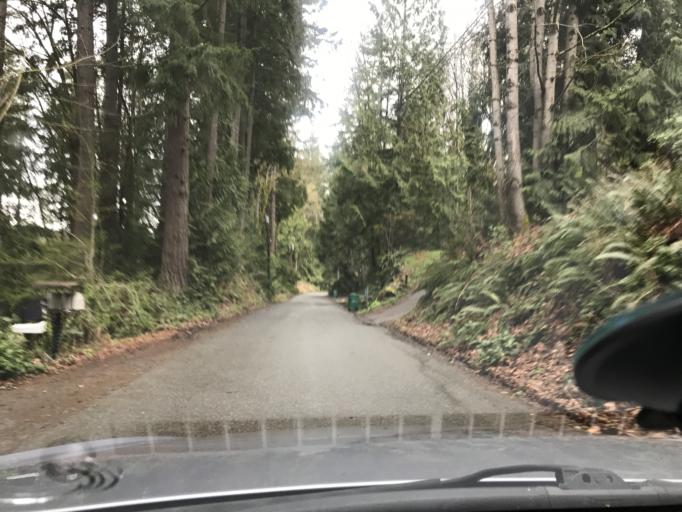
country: US
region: Washington
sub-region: King County
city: Ames Lake
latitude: 47.6427
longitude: -121.9537
